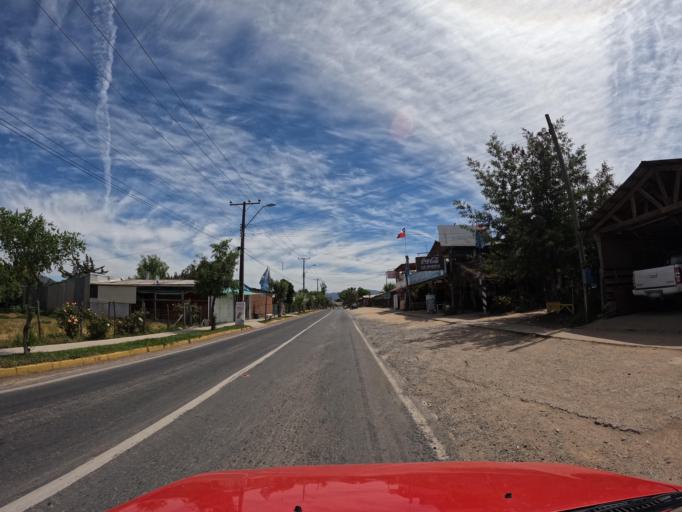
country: CL
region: Maule
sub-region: Provincia de Talca
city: Talca
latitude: -35.0896
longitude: -71.6524
